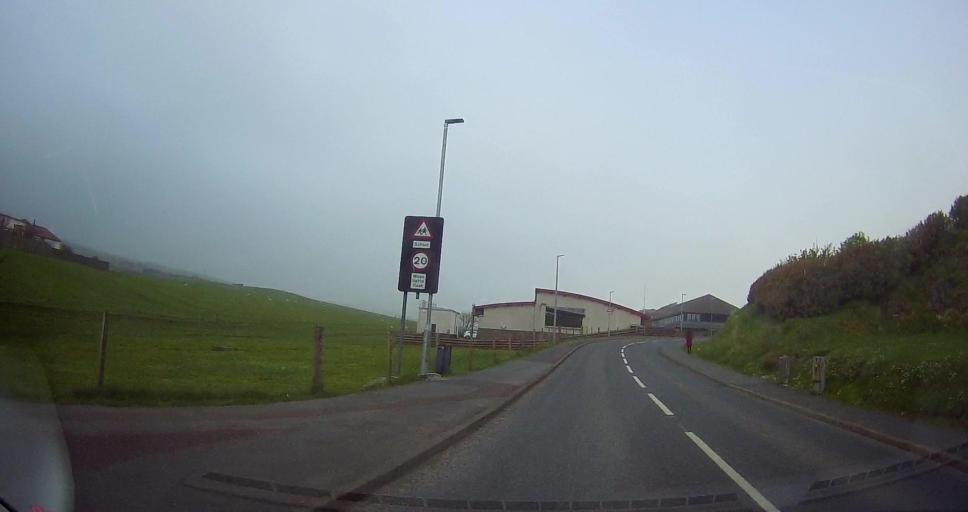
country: GB
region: Scotland
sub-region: Shetland Islands
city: Lerwick
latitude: 60.1389
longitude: -1.2741
